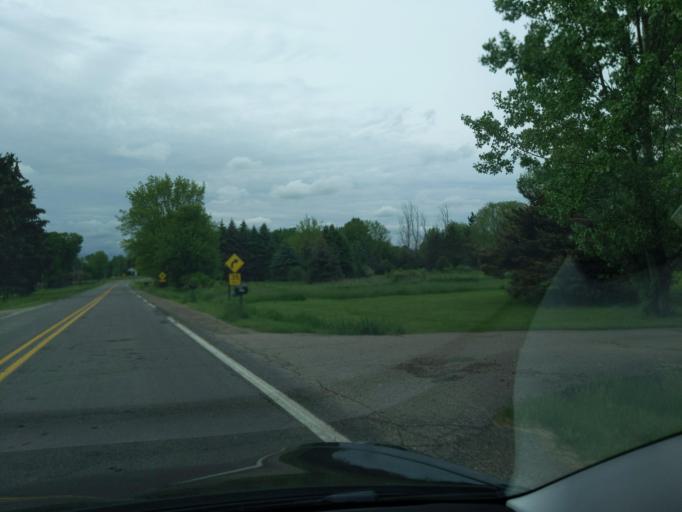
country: US
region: Michigan
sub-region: Ingham County
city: Mason
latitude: 42.6092
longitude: -84.4552
